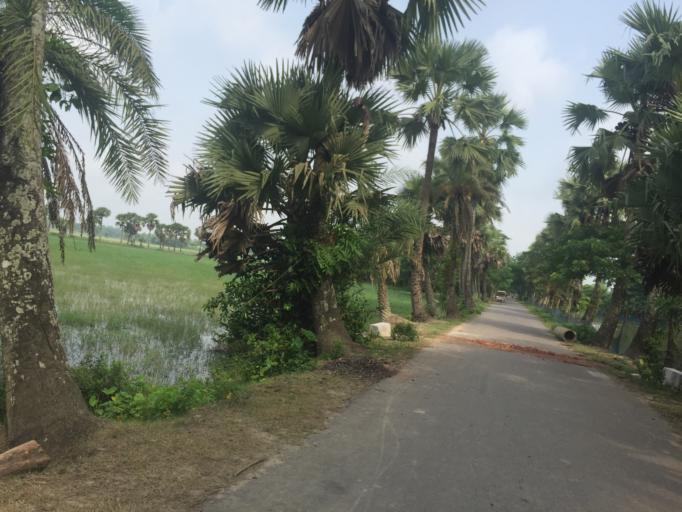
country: BD
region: Barisal
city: Mathba
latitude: 22.2096
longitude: 89.9311
